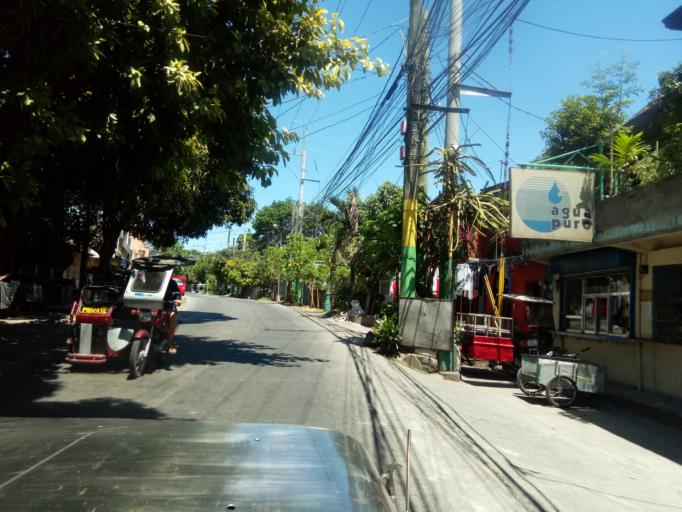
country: PH
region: Calabarzon
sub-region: Province of Cavite
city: Dasmarinas
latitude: 14.3195
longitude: 120.9695
